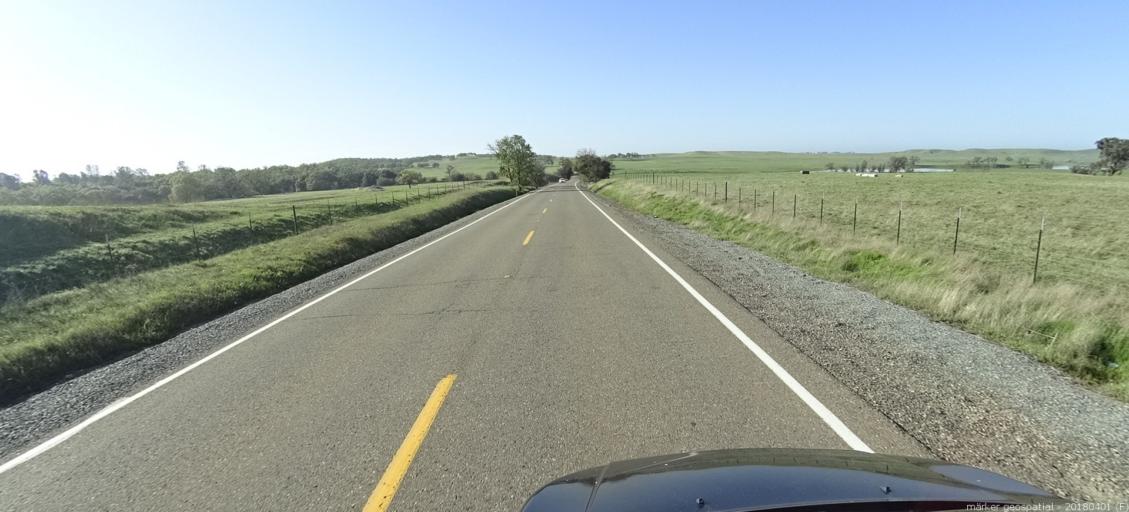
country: US
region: California
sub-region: Sacramento County
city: Rancho Murieta
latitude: 38.4763
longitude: -121.0439
